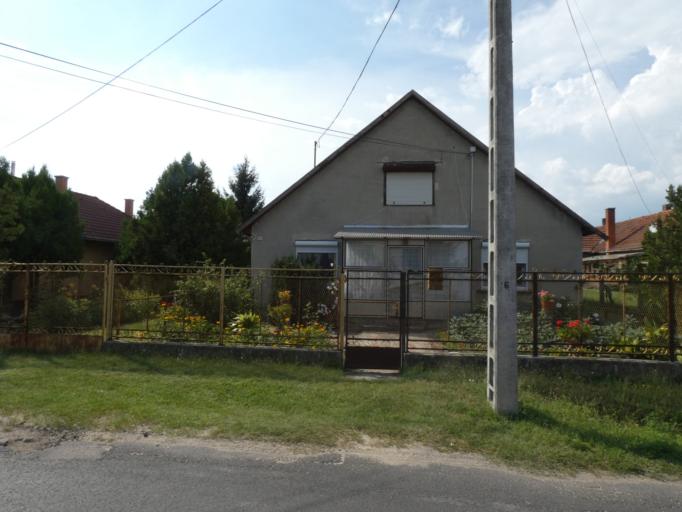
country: HU
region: Pest
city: Taborfalva
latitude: 47.1066
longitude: 19.4869
